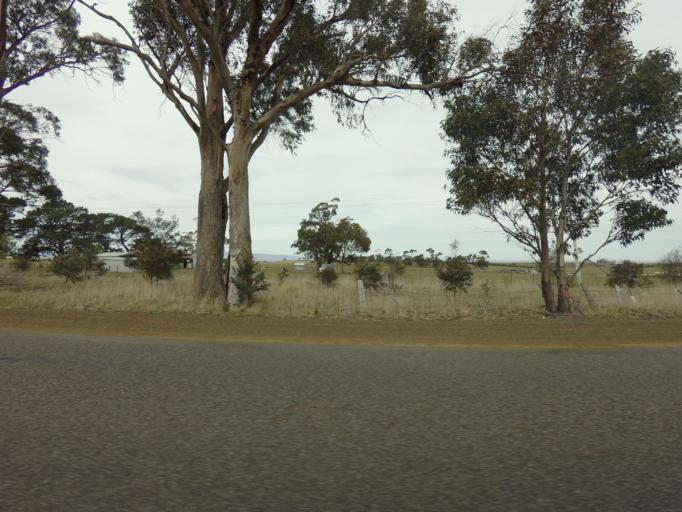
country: AU
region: Tasmania
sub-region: Sorell
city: Sorell
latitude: -42.2550
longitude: 148.0055
